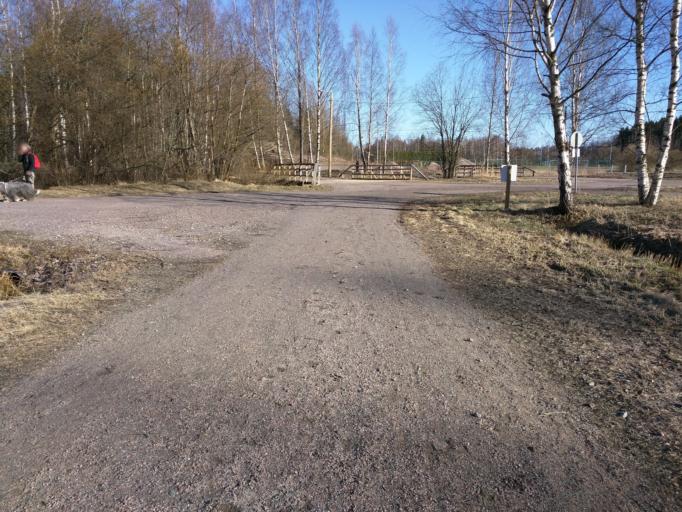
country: FI
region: Uusimaa
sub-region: Helsinki
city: Kilo
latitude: 60.2281
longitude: 24.7932
